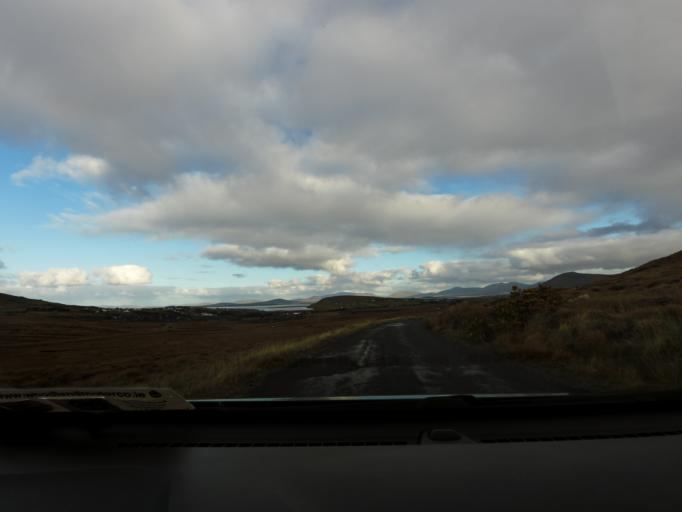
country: IE
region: Connaught
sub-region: Maigh Eo
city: Belmullet
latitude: 53.9419
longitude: -9.9835
